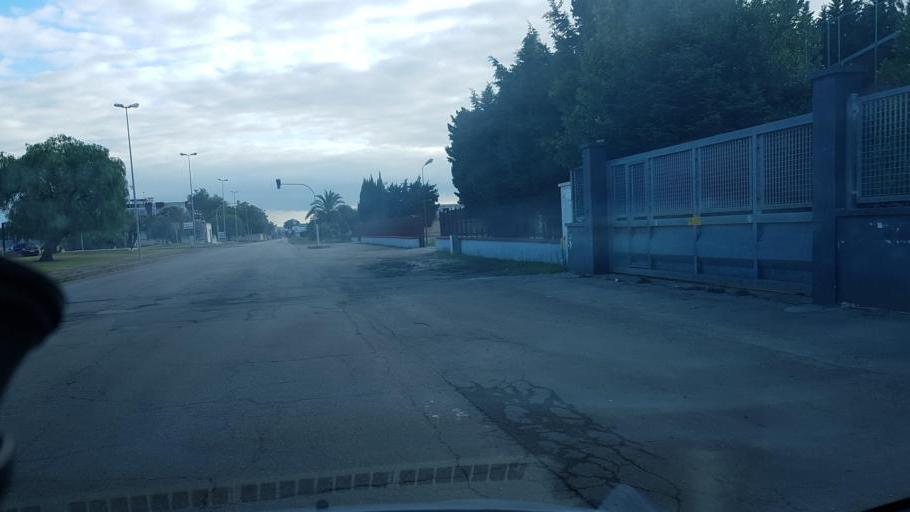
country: IT
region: Apulia
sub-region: Provincia di Lecce
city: Veglie
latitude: 40.3469
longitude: 17.9691
